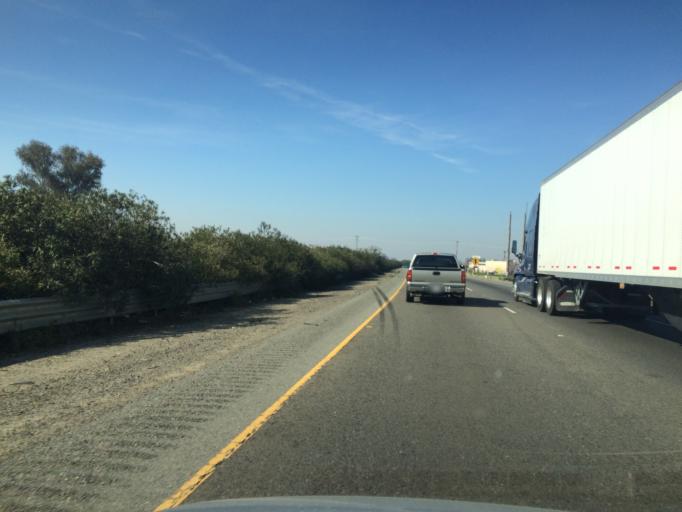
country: US
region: California
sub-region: Tulare County
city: Tulare
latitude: 36.2398
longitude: -119.3452
